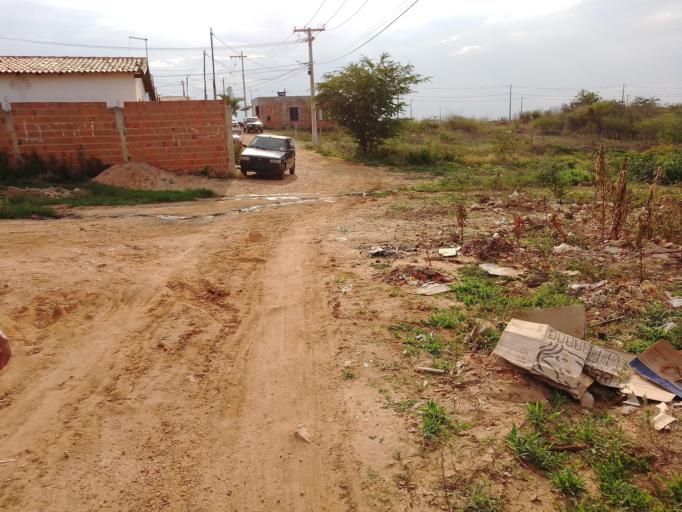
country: BR
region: Bahia
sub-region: Brumado
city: Brumado
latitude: -14.4412
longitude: -41.4629
